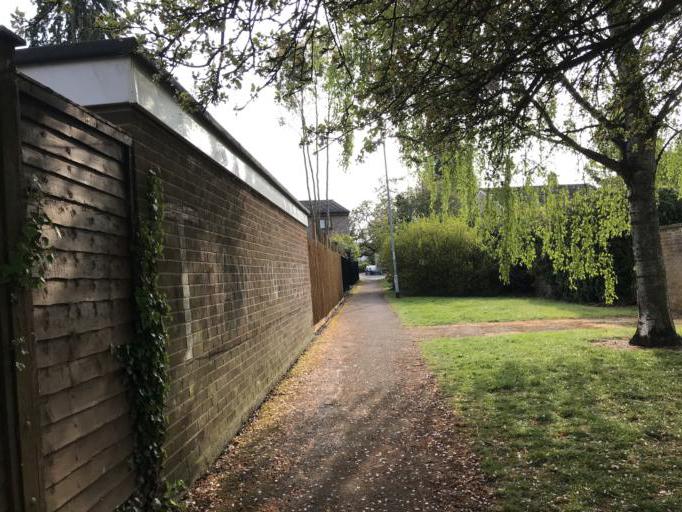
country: GB
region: England
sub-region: Cambridgeshire
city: Cambridge
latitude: 52.1760
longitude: 0.1533
